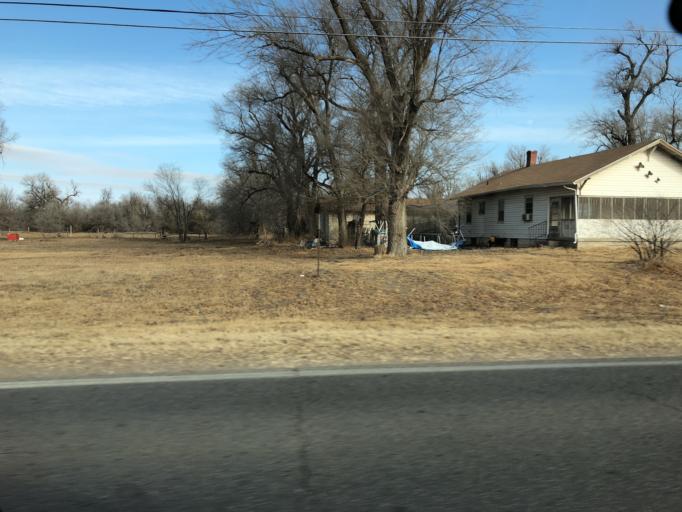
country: US
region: Kansas
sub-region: Reno County
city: South Hutchinson
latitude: 38.0574
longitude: -97.9825
